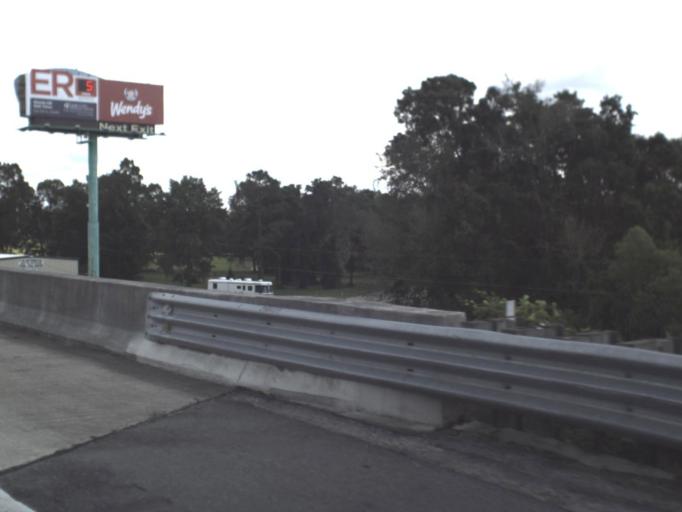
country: US
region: Florida
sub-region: Columbia County
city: Lake City
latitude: 30.1462
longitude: -82.6713
